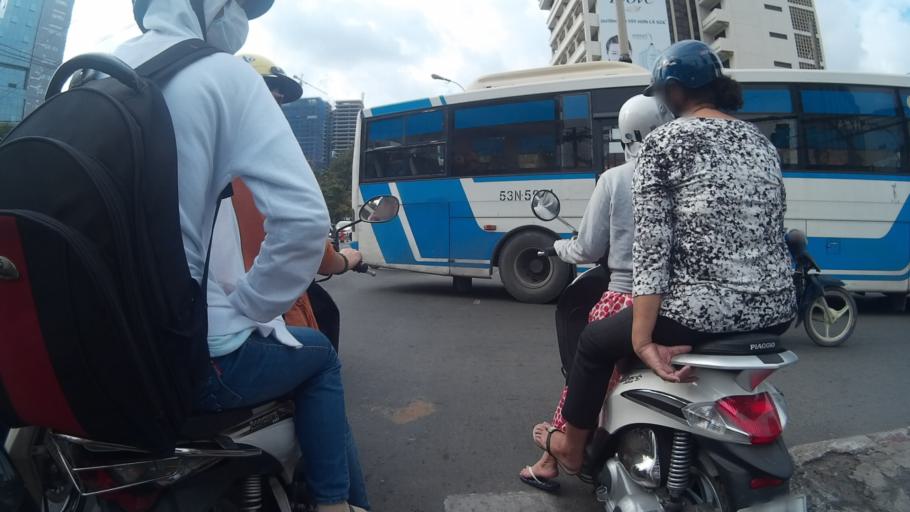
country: VN
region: Ho Chi Minh City
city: Quan Ba
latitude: 10.7767
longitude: 106.6839
